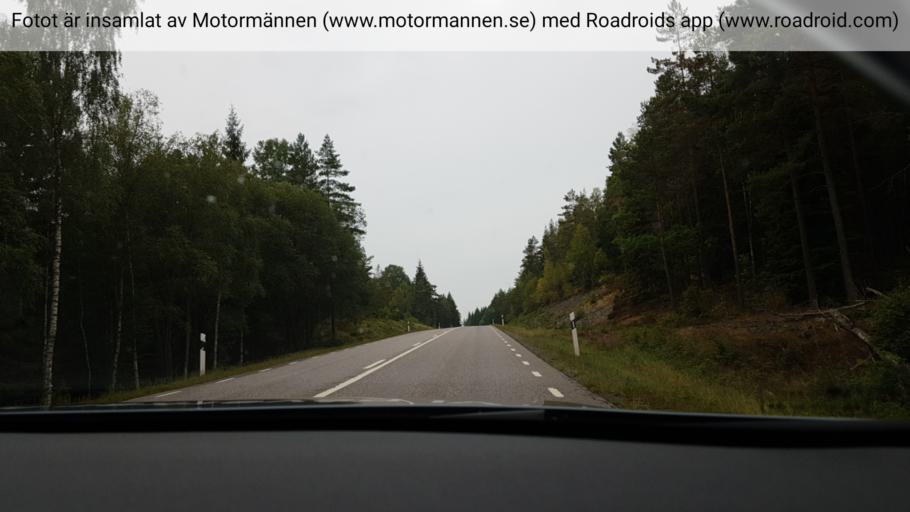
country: SE
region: Joenkoeping
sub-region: Varnamo Kommun
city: Bor
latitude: 57.2430
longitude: 14.1684
